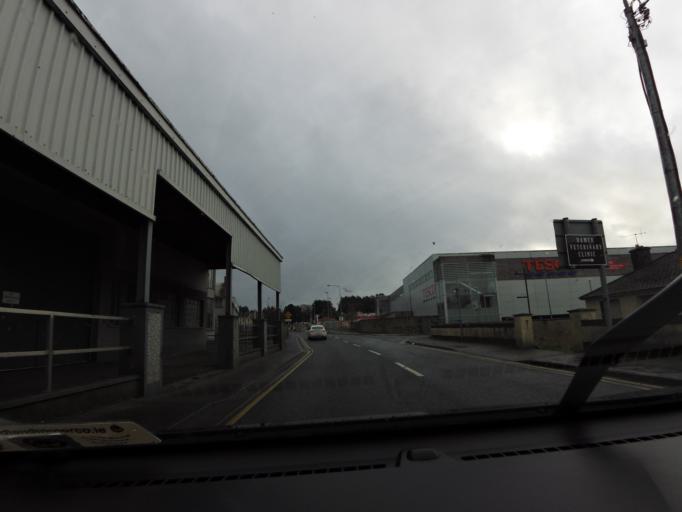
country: IE
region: Munster
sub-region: North Tipperary
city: Roscrea
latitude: 52.9573
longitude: -7.7967
